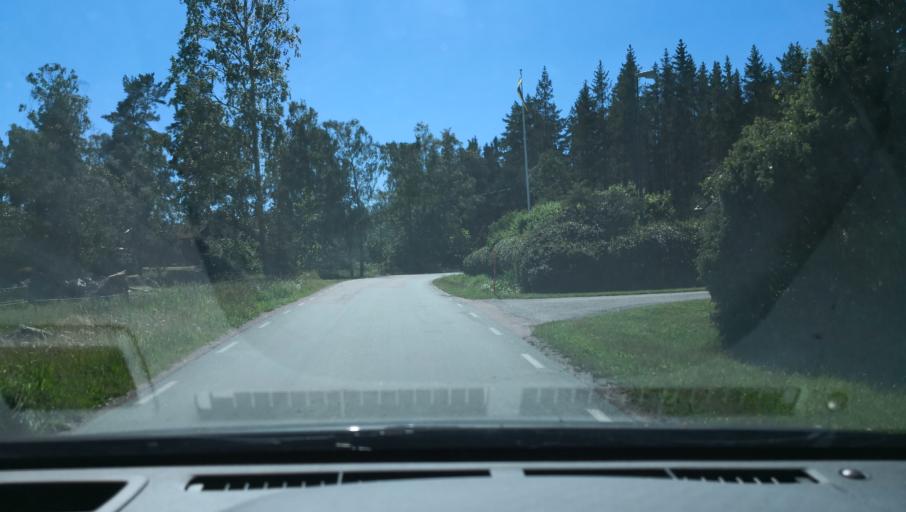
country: SE
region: Soedermanland
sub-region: Eskilstuna Kommun
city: Hallbybrunn
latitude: 59.3084
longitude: 16.3738
